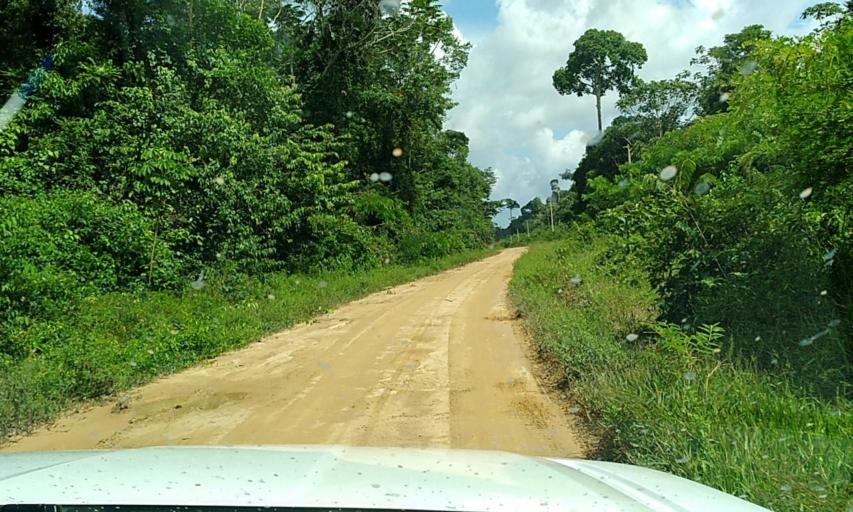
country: BR
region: Para
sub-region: Senador Jose Porfirio
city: Senador Jose Porfirio
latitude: -2.5228
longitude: -51.8322
